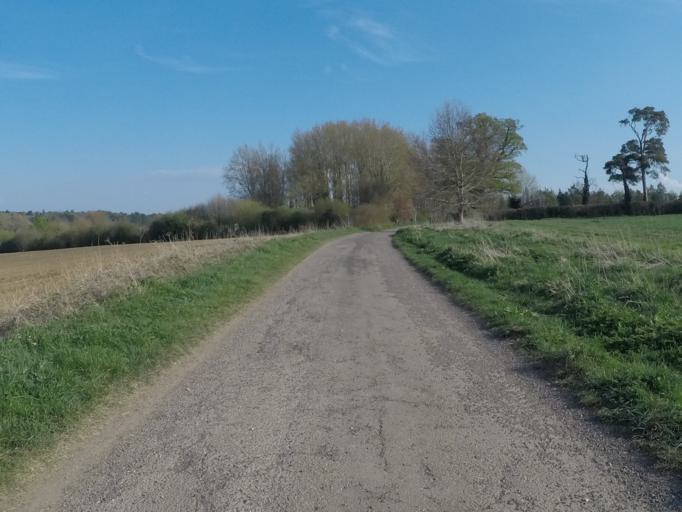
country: GB
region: England
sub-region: Oxfordshire
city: Charlbury
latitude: 51.8736
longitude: -1.4952
